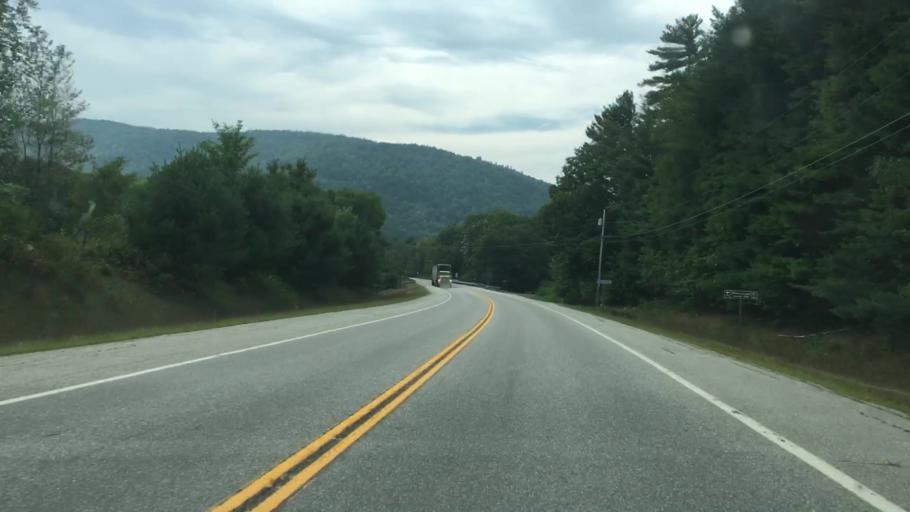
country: US
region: Maine
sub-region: Oxford County
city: Bethel
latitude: 44.4889
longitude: -70.7803
